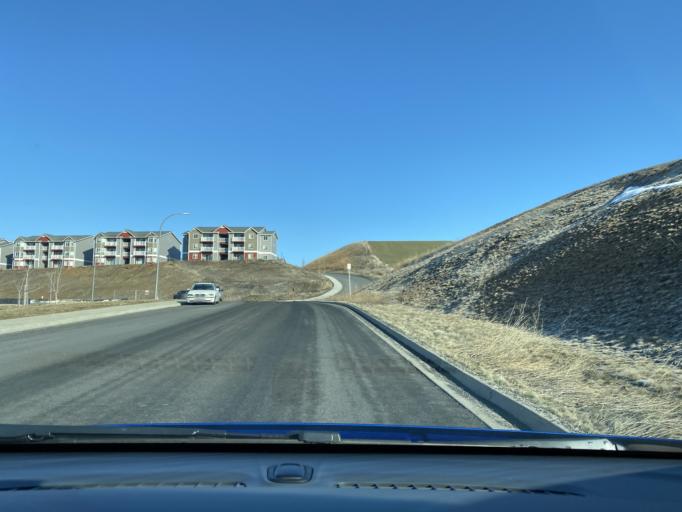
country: US
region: Washington
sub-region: Whitman County
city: Pullman
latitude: 46.7471
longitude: -117.1453
